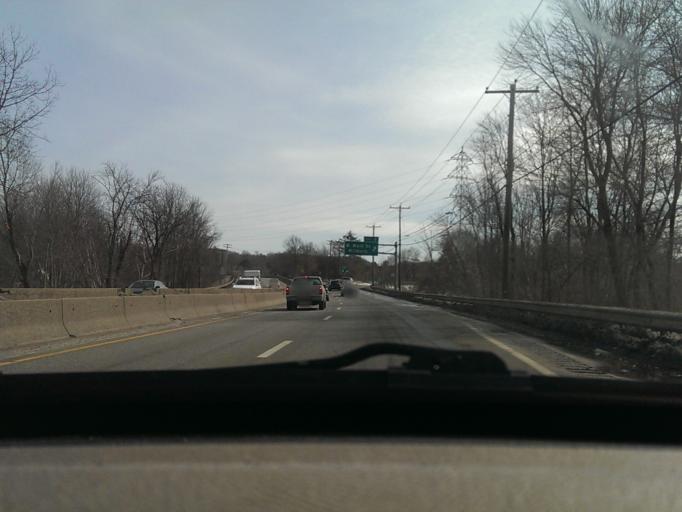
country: US
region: Massachusetts
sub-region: Worcester County
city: Millbury
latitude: 42.1893
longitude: -71.7686
